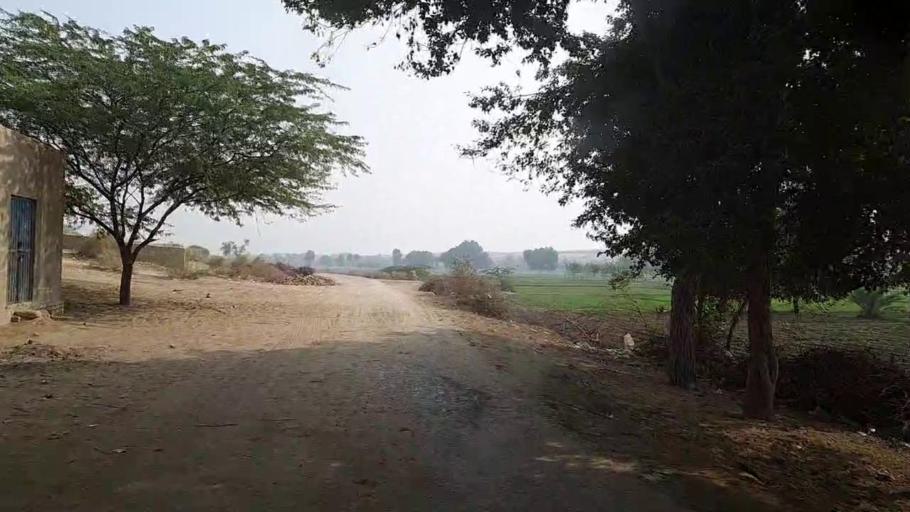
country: PK
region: Sindh
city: Bozdar
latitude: 27.0588
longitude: 68.6537
